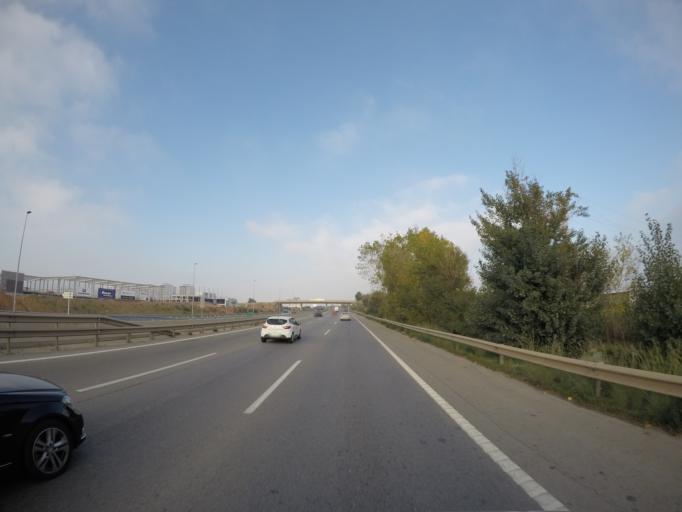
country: ES
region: Catalonia
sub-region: Provincia de Barcelona
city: Viladecans
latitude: 41.3055
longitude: 2.0268
